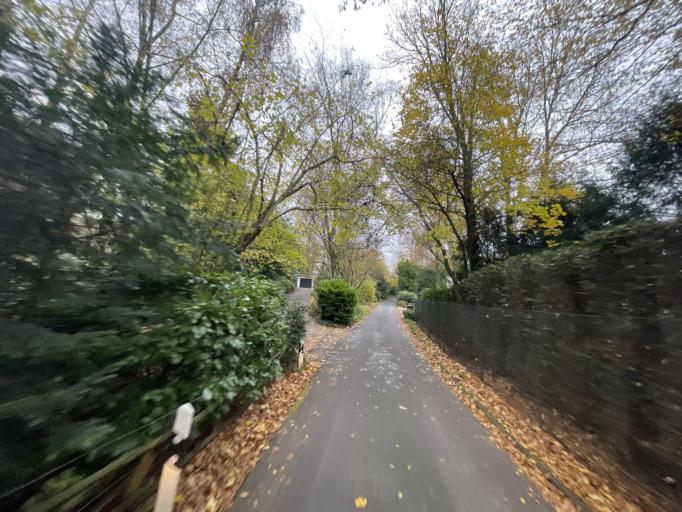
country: DE
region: North Rhine-Westphalia
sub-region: Regierungsbezirk Dusseldorf
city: Erkrath
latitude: 51.2629
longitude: 6.9200
